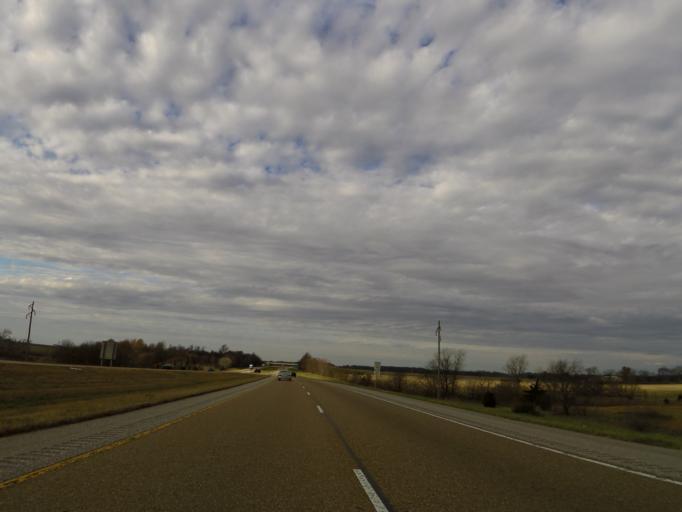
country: US
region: Illinois
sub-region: Clinton County
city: Wamac
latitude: 38.3901
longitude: -89.1808
